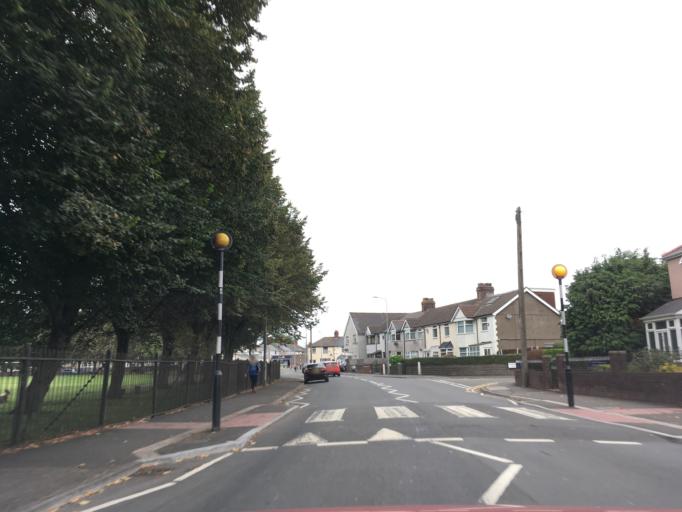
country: GB
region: Wales
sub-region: Cardiff
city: Cardiff
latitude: 51.4852
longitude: -3.1431
